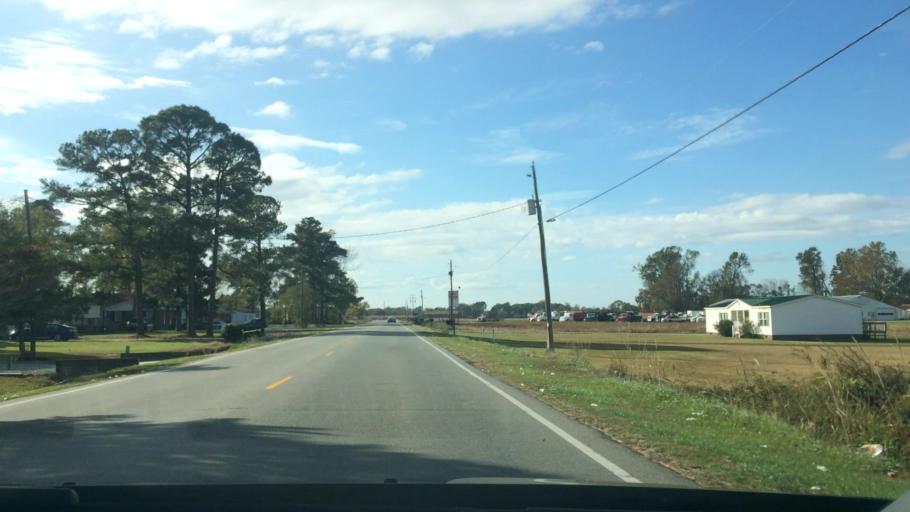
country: US
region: North Carolina
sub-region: Wayne County
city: Elroy
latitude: 35.4410
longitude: -77.8381
